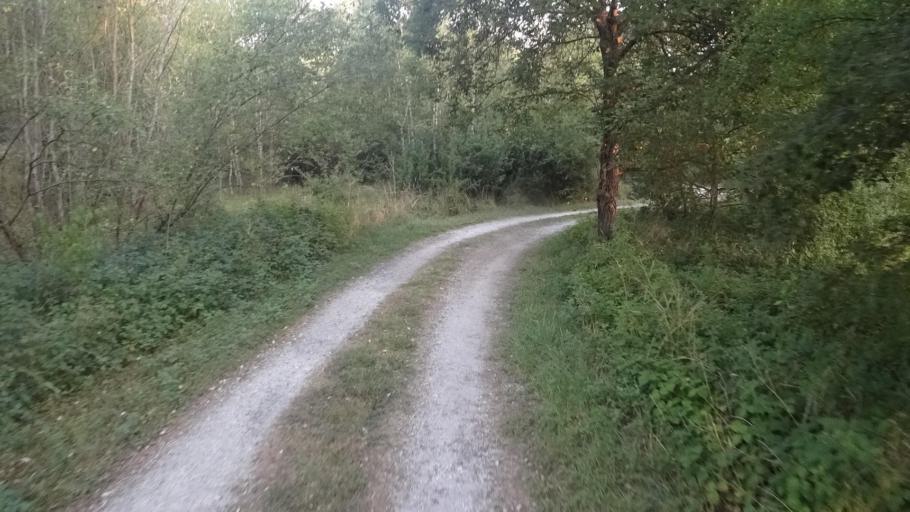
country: DE
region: Rheinland-Pfalz
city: Kumbdchen
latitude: 49.9763
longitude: 7.5141
